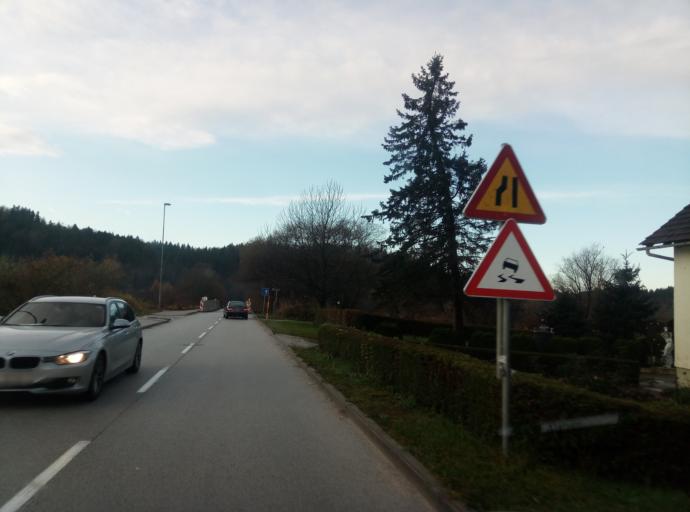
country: SI
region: Menges
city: Menges
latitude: 46.1746
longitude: 14.5633
